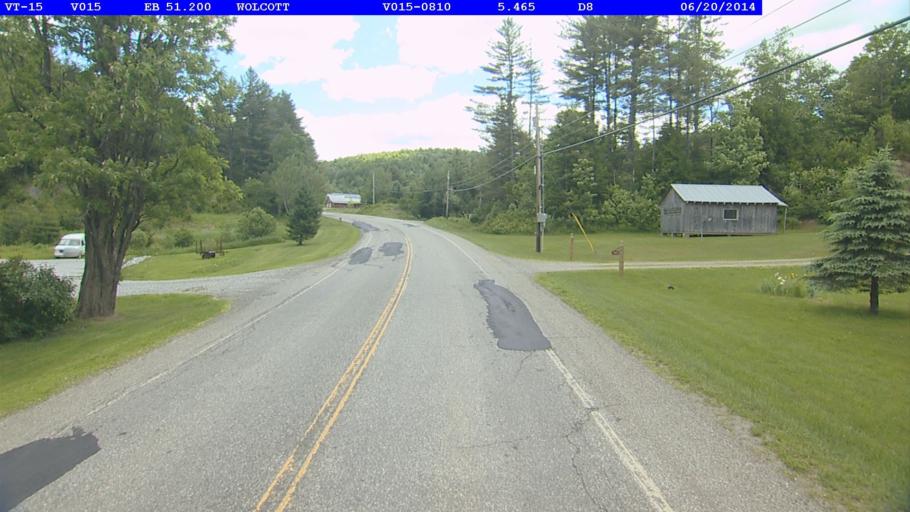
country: US
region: Vermont
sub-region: Caledonia County
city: Hardwick
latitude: 44.5346
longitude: -72.4435
